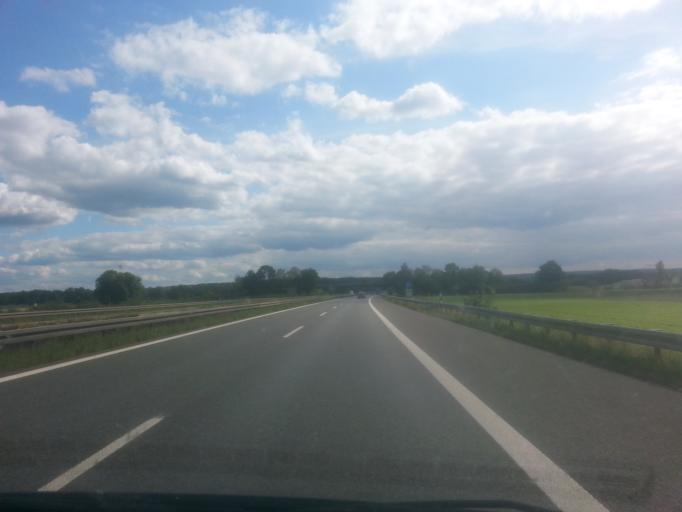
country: DE
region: Bavaria
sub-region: Upper Palatinate
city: Schwarzenfeld
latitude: 49.3760
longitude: 12.1513
